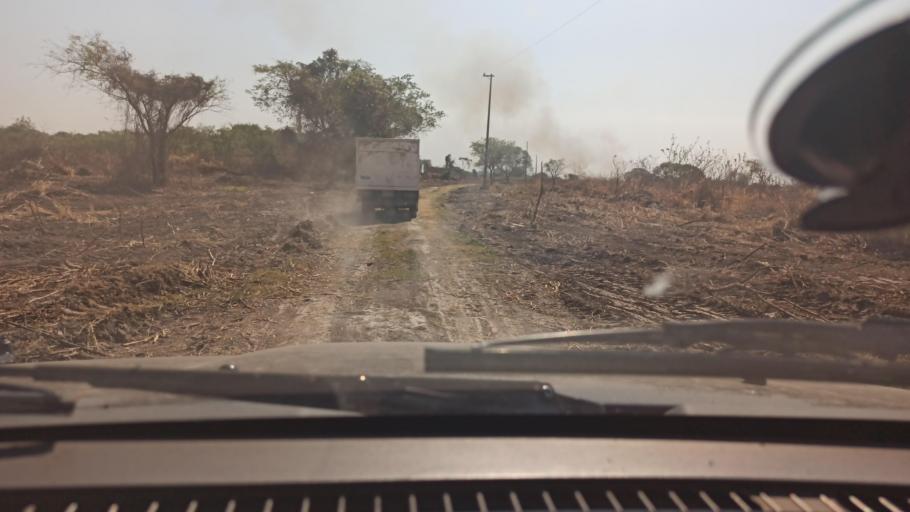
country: PY
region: Asuncion
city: Asuncion
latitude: -25.3451
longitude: -57.6755
